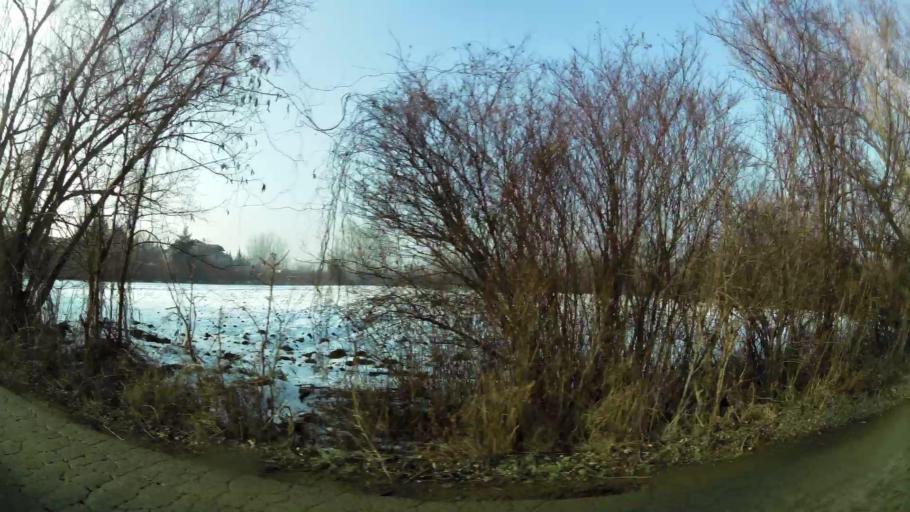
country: MK
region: Ilinden
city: Idrizovo
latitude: 41.9595
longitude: 21.5886
